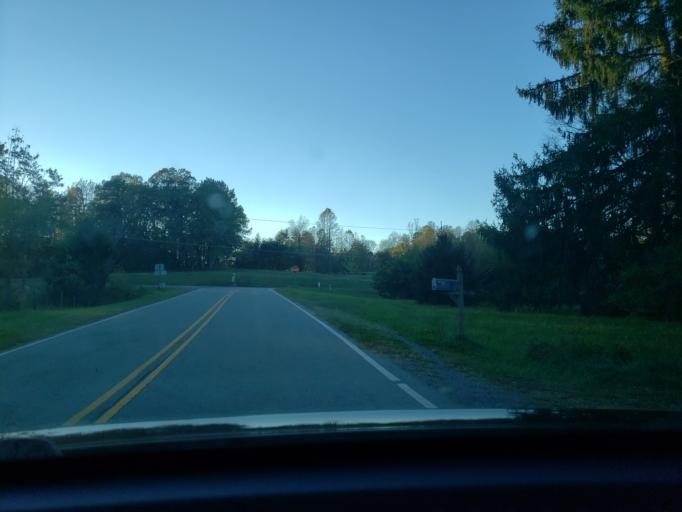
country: US
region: North Carolina
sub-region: Forsyth County
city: Walkertown
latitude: 36.2256
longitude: -80.1981
